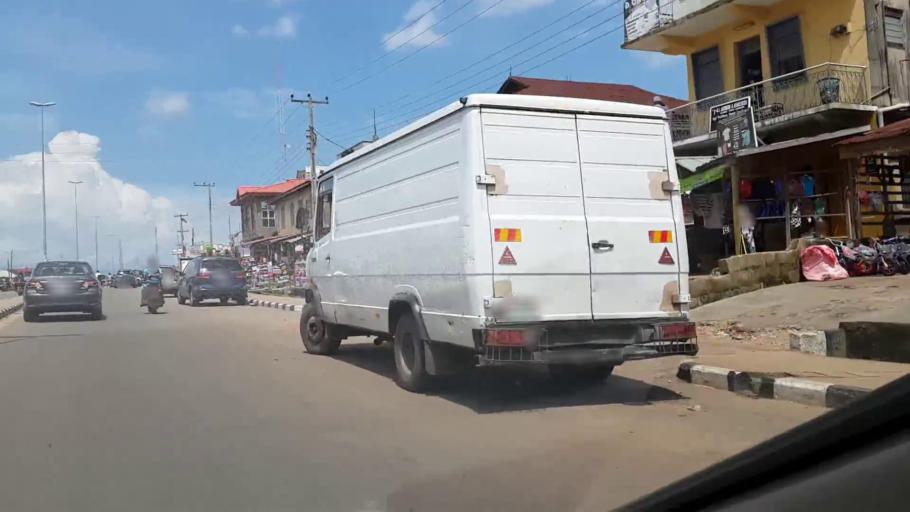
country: NG
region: Ondo
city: Ondo
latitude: 7.1009
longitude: 4.8441
